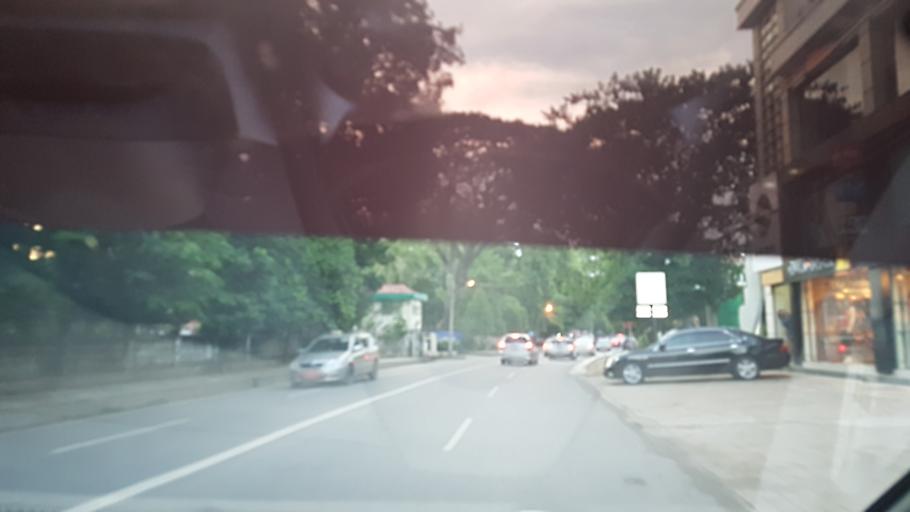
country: MM
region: Yangon
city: Yangon
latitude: 16.8090
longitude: 96.1435
